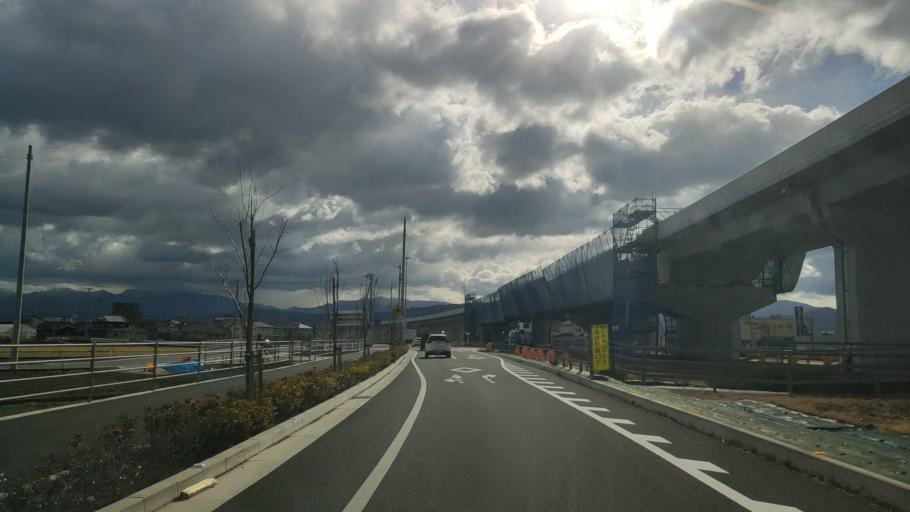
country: JP
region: Ehime
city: Masaki-cho
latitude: 33.8141
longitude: 132.7211
